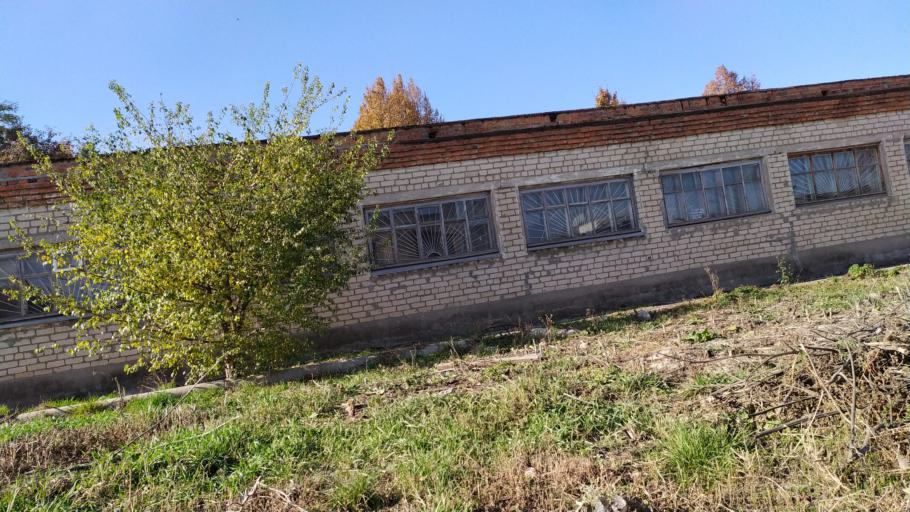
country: RU
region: Kursk
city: Kursk
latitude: 51.6544
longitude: 36.1541
